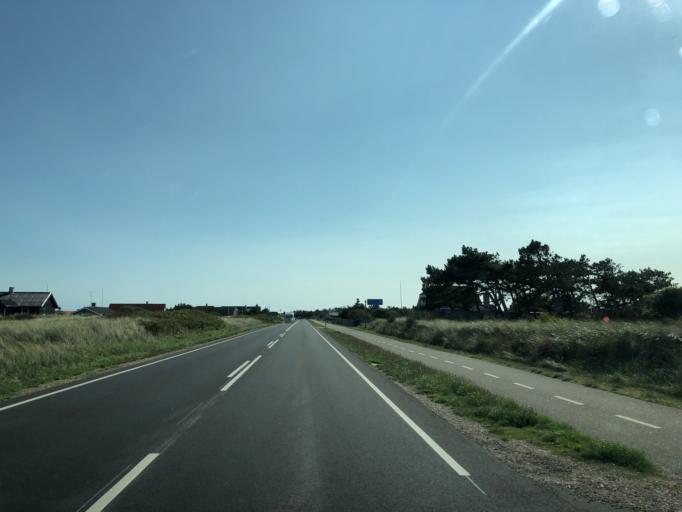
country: DK
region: Central Jutland
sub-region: Ringkobing-Skjern Kommune
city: Hvide Sande
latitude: 56.0565
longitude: 8.1206
